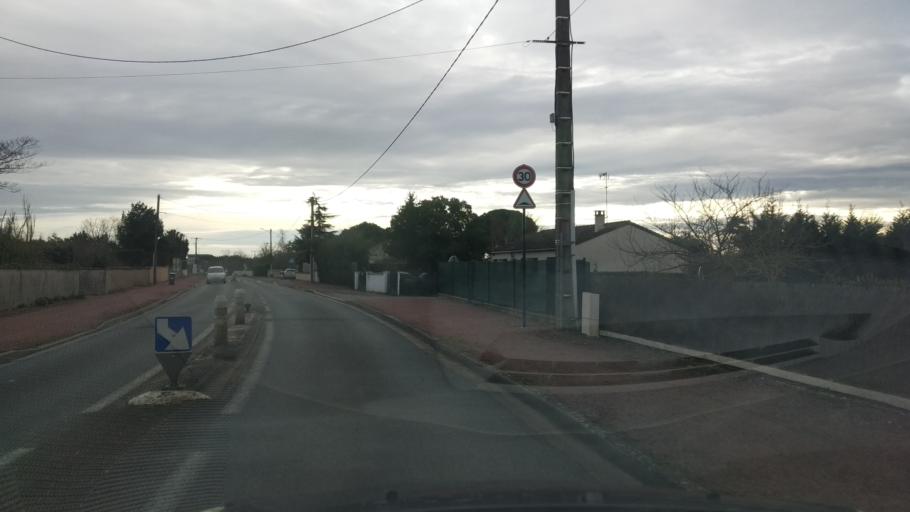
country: FR
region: Poitou-Charentes
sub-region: Departement de la Vienne
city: Dissay
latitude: 46.6894
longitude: 0.4165
